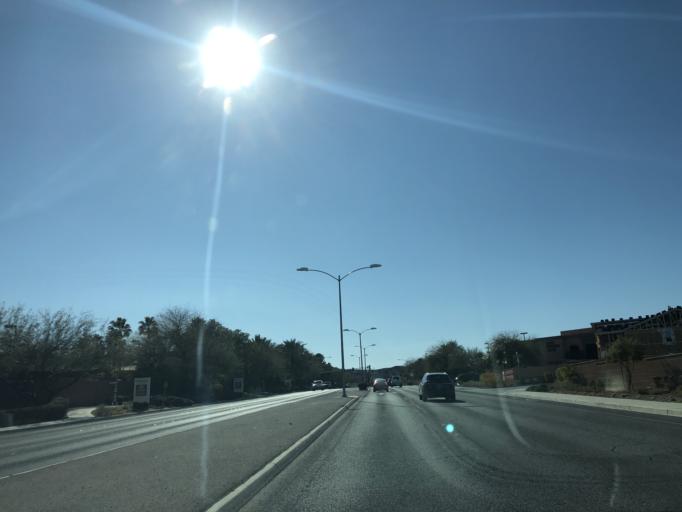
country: US
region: Nevada
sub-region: Clark County
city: Whitney
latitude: 36.0132
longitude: -115.0602
